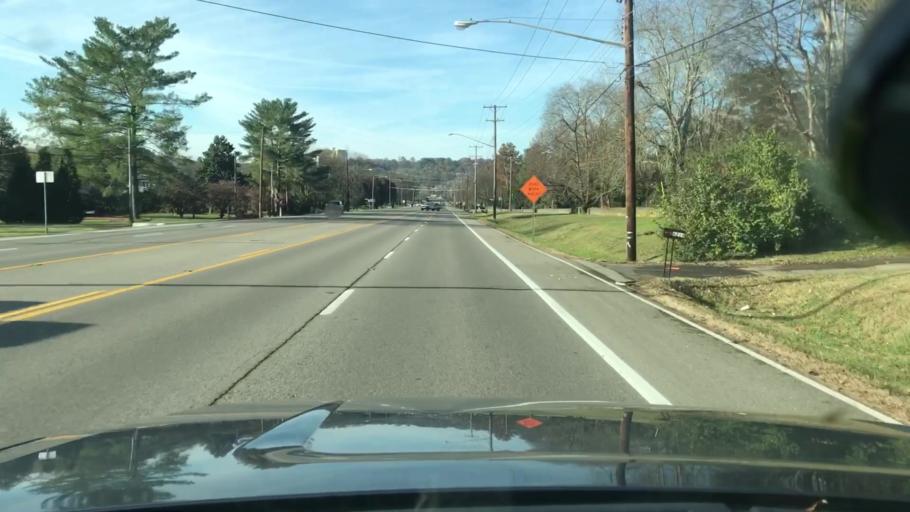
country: US
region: Tennessee
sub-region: Davidson County
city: Belle Meade
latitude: 36.0953
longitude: -86.8800
